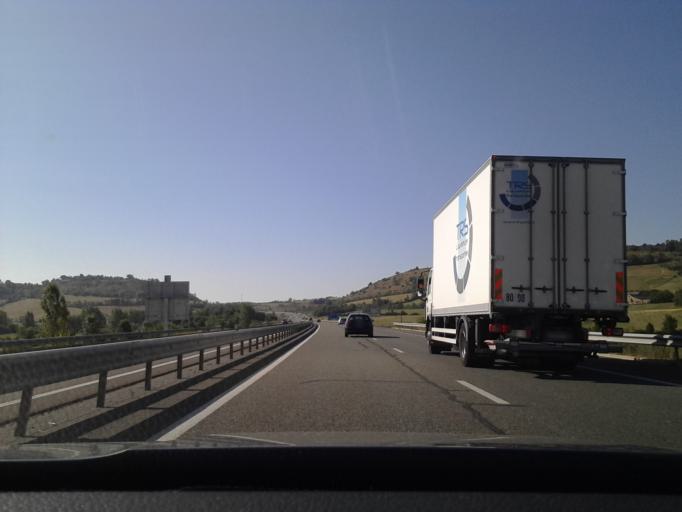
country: FR
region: Midi-Pyrenees
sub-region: Departement de l'Aveyron
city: Severac-le-Chateau
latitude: 44.3258
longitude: 3.0883
